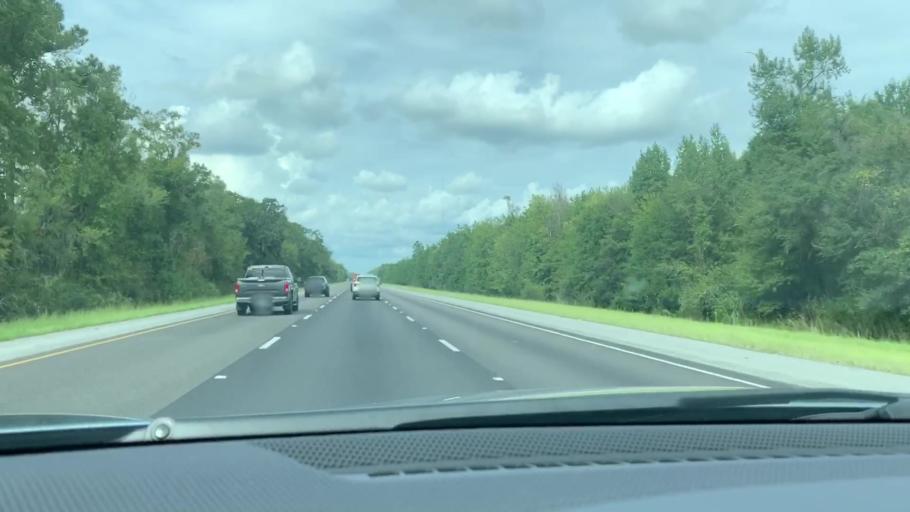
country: US
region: Georgia
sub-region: Liberty County
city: Midway
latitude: 31.6845
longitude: -81.3915
